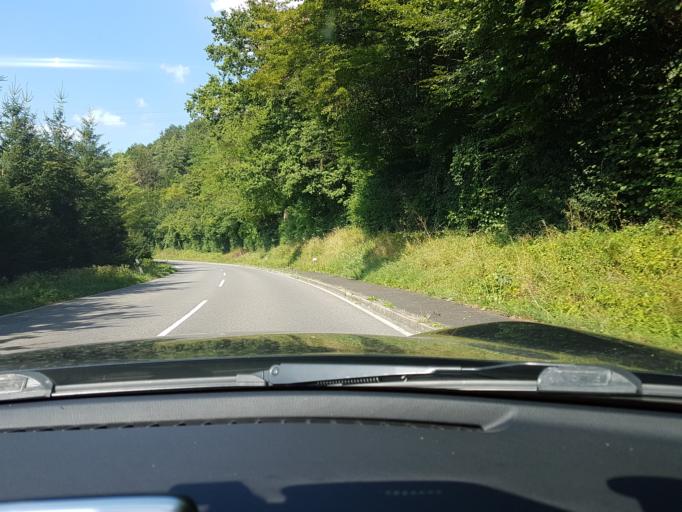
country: DE
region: Baden-Wuerttemberg
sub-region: Regierungsbezirk Stuttgart
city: Mockmuhl
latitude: 49.3300
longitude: 9.3542
